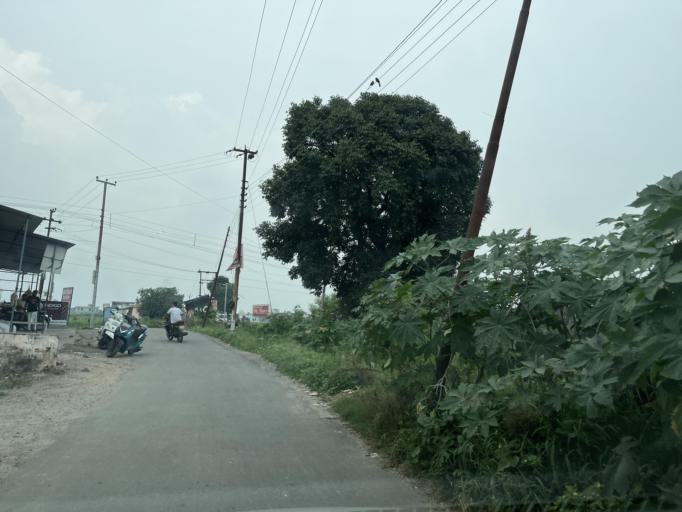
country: IN
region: Uttarakhand
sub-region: Naini Tal
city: Haldwani
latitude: 29.1725
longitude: 79.4857
